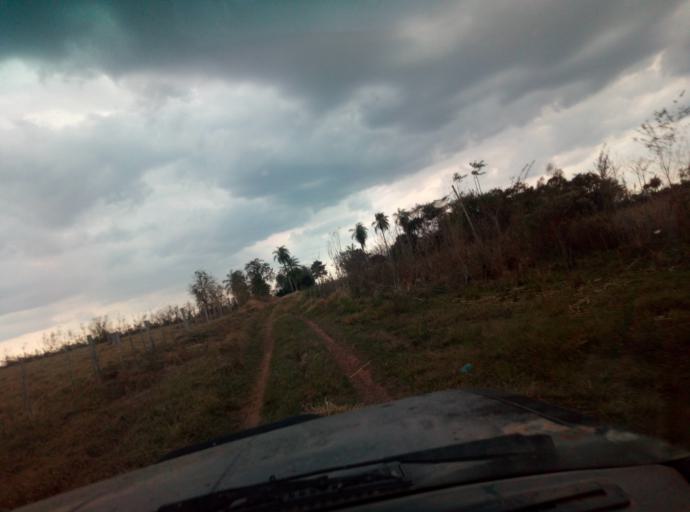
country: PY
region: Caaguazu
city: Doctor Cecilio Baez
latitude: -25.1464
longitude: -56.2244
